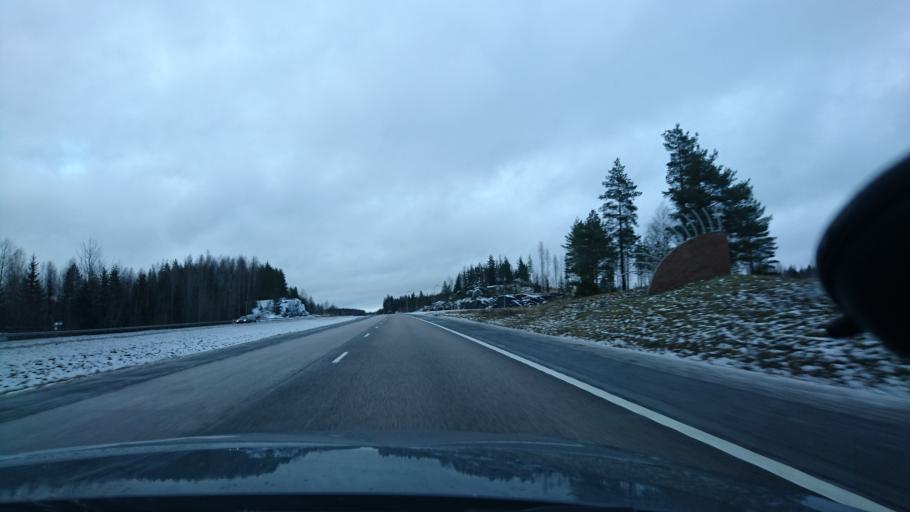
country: FI
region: Uusimaa
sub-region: Porvoo
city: Pukkila
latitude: 60.7675
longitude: 25.4685
